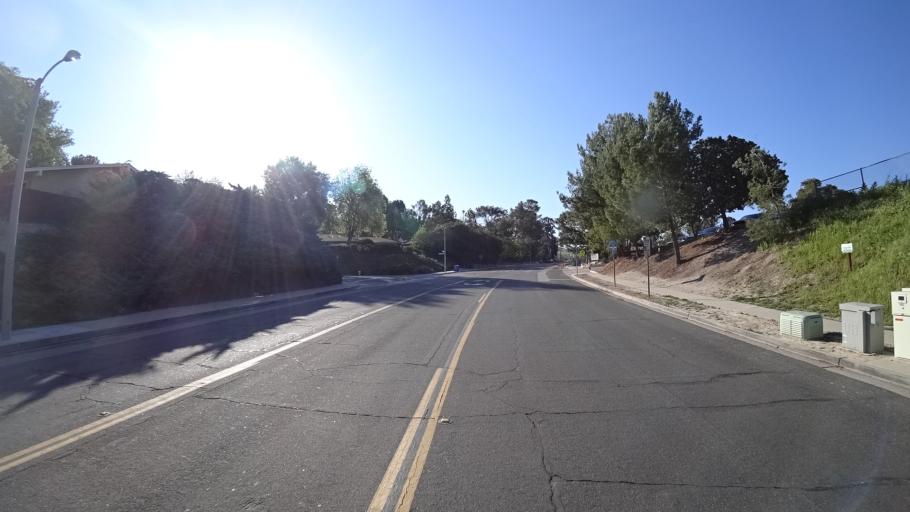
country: US
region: California
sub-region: Ventura County
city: Thousand Oaks
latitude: 34.1936
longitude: -118.8416
